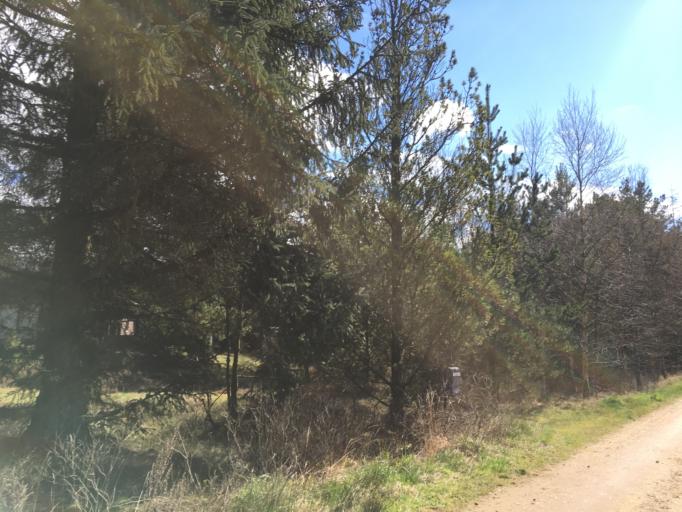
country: DK
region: South Denmark
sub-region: Varde Kommune
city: Oksbol
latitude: 55.5606
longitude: 8.2208
